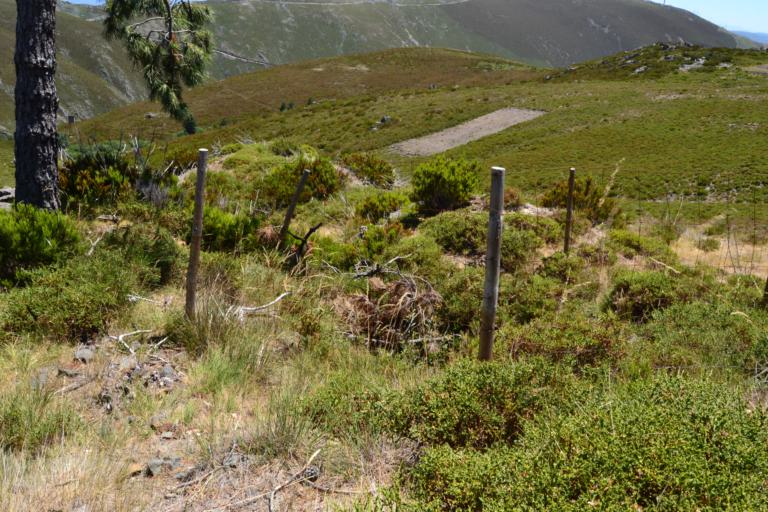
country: PT
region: Vila Real
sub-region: Mesao Frio
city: Mesao Frio
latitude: 41.2353
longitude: -7.9040
